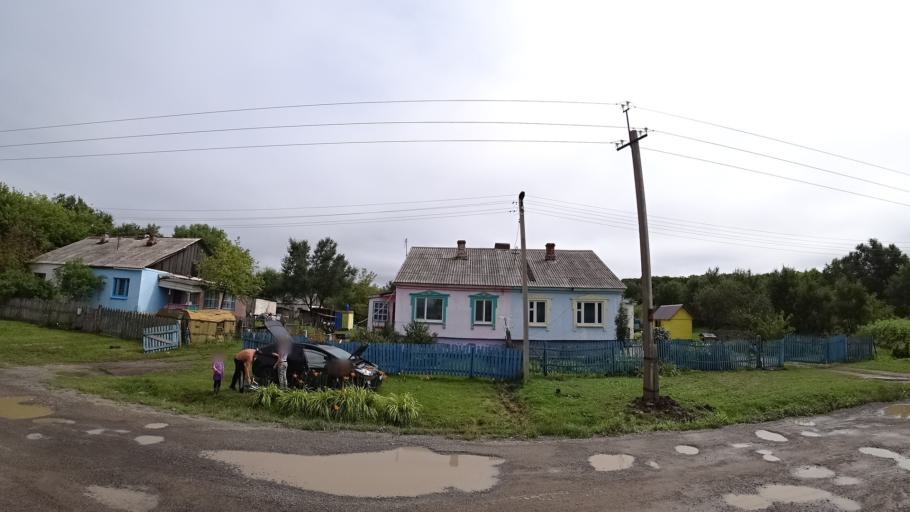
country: RU
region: Primorskiy
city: Lyalichi
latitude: 44.0757
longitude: 132.4708
